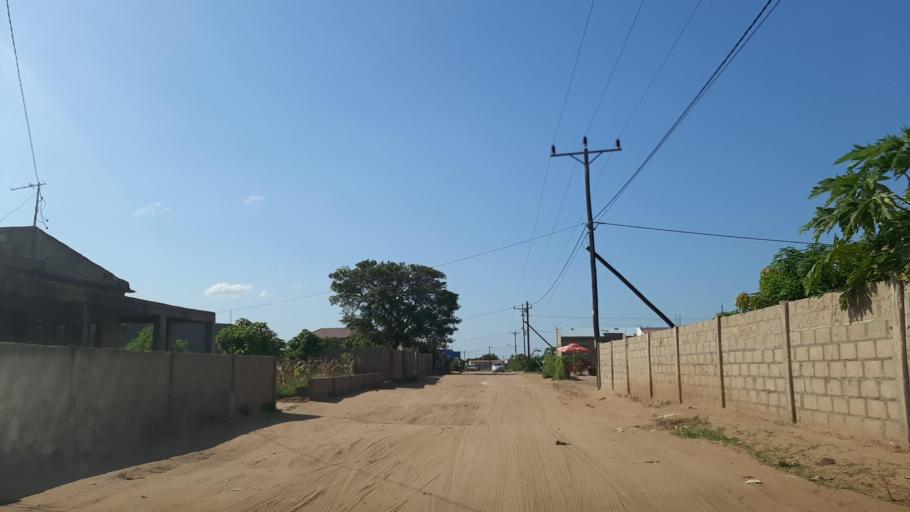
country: MZ
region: Maputo
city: Matola
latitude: -25.8014
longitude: 32.4910
